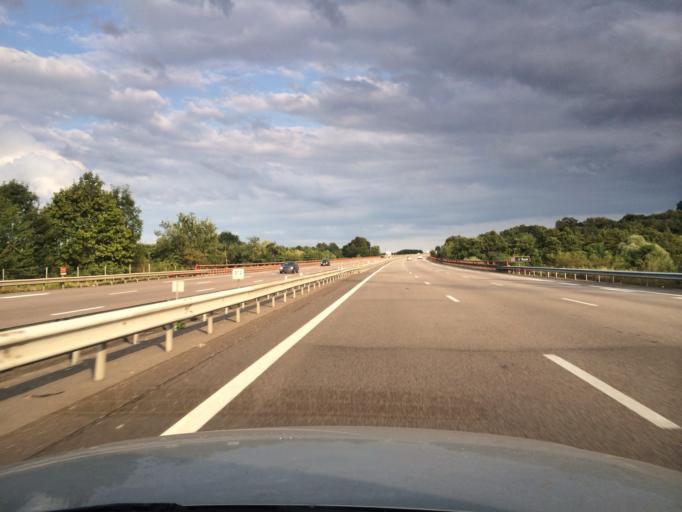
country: FR
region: Haute-Normandie
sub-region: Departement de l'Eure
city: Le Vaudreuil
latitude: 49.2430
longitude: 1.1909
